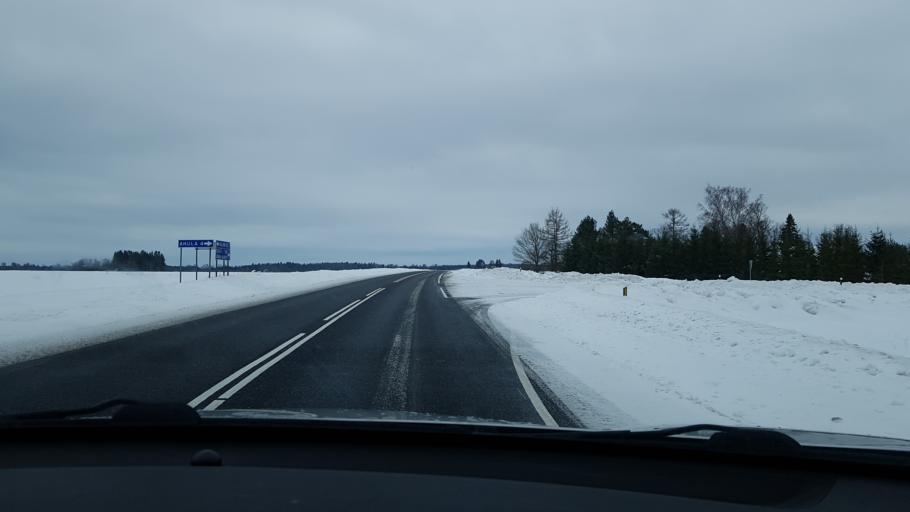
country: EE
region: Jaervamaa
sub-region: Jaerva-Jaani vald
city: Jarva-Jaani
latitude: 59.1172
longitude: 25.7923
